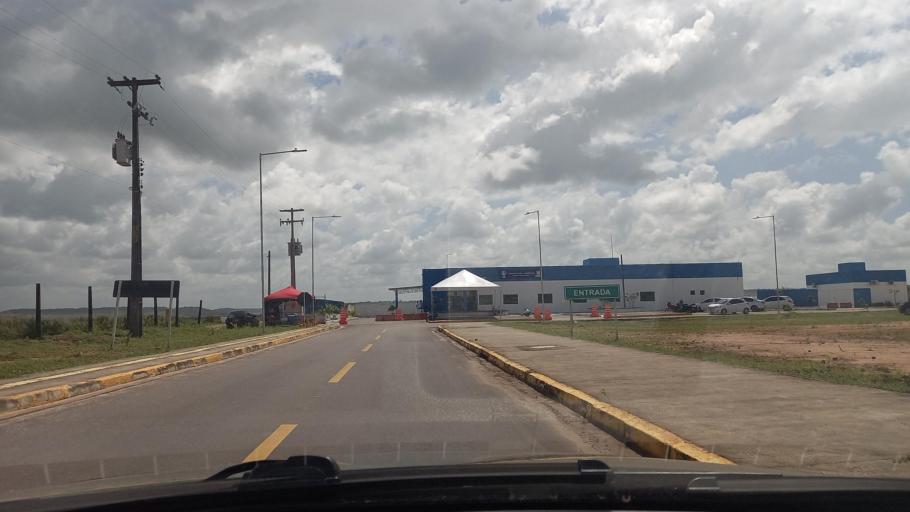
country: BR
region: Pernambuco
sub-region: Goiana
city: Goiana
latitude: -7.5548
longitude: -35.0209
